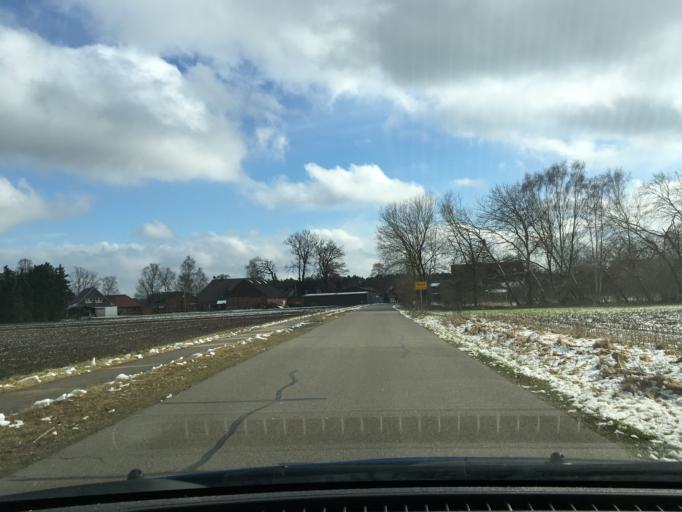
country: DE
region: Lower Saxony
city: Handorf
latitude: 53.3290
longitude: 10.3543
